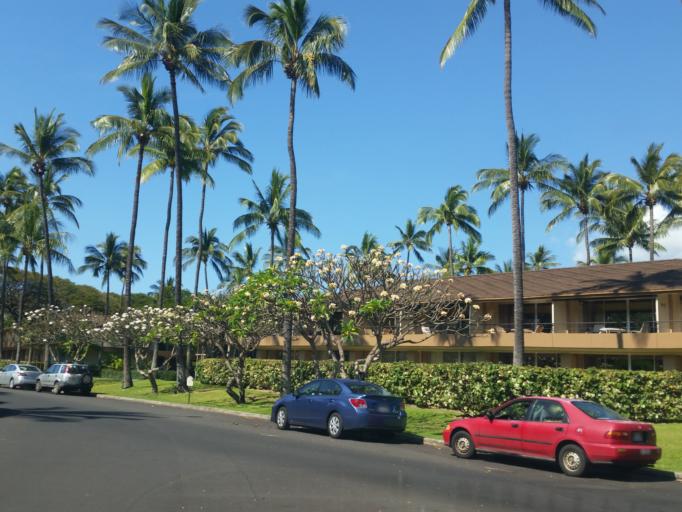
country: US
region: Hawaii
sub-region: Maui County
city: Kaanapali Landing
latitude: 20.9347
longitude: -156.6915
